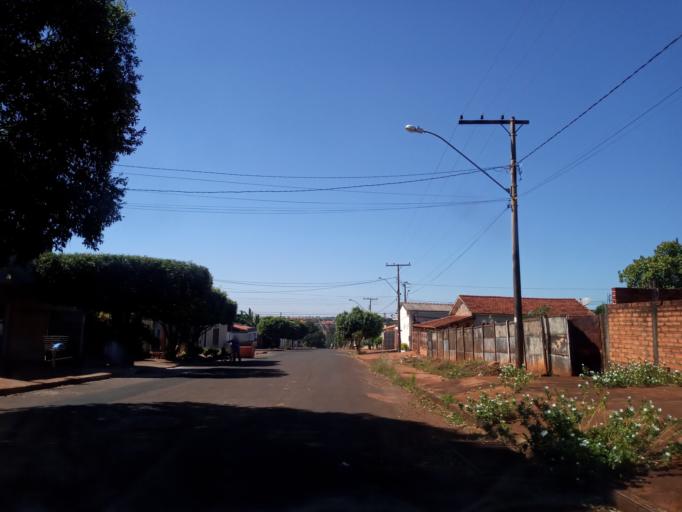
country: BR
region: Minas Gerais
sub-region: Ituiutaba
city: Ituiutaba
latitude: -18.9900
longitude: -49.4494
